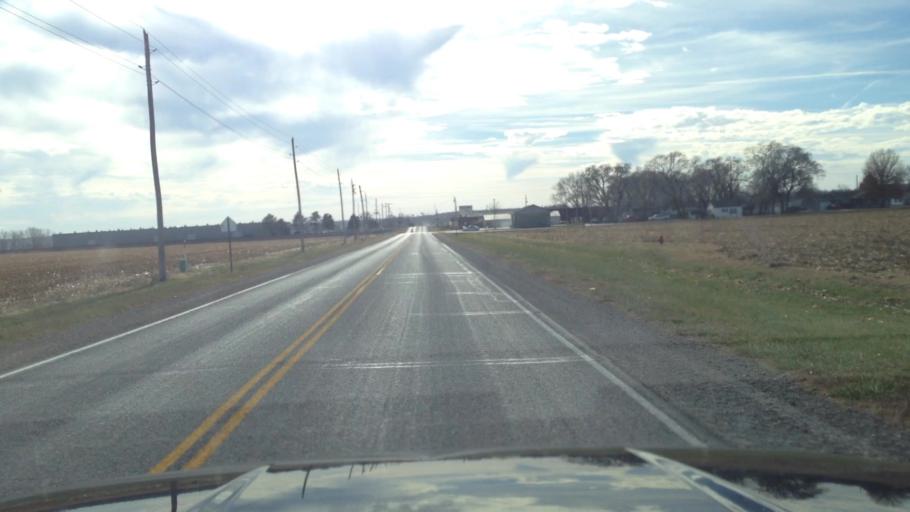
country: US
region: Kansas
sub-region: Jefferson County
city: Oskaloosa
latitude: 39.0751
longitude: -95.3820
